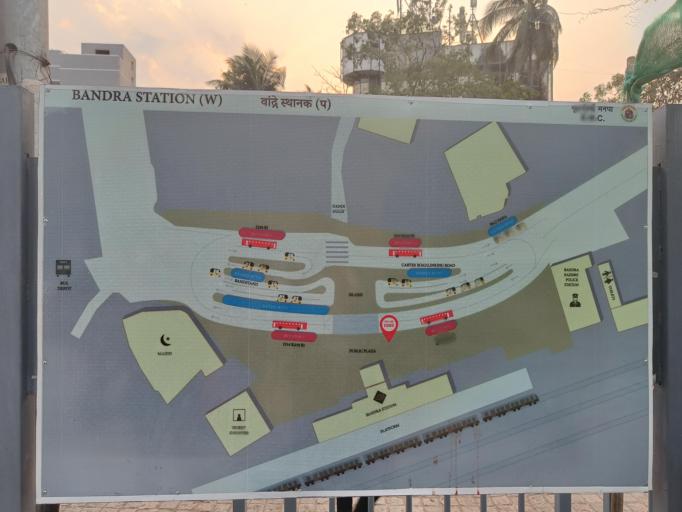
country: IN
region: Maharashtra
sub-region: Mumbai Suburban
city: Mumbai
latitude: 19.0560
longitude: 72.8393
